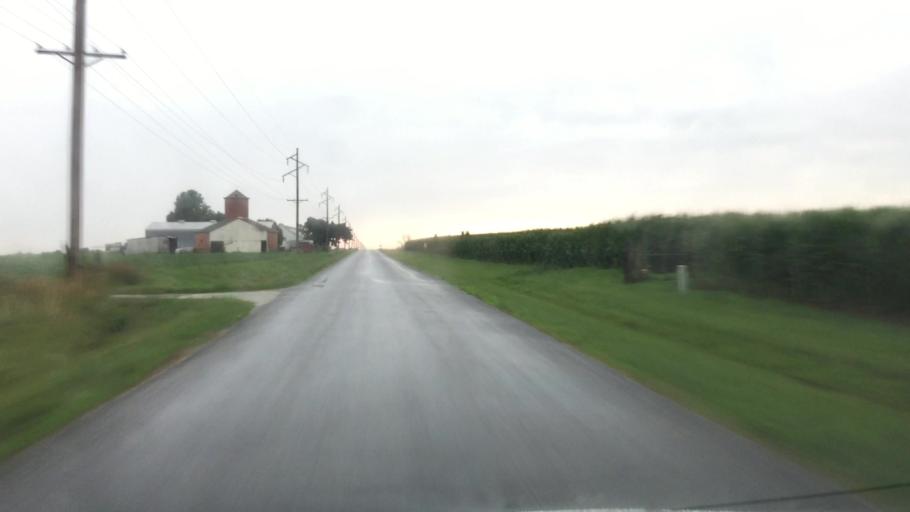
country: US
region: Illinois
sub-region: Hancock County
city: Hamilton
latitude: 40.4989
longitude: -91.2699
